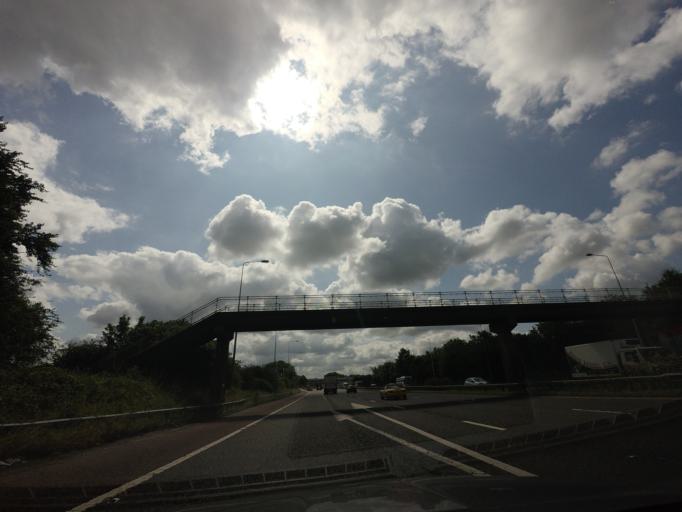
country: GB
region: England
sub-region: Lancashire
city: Coppull
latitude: 53.6346
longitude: -2.6915
